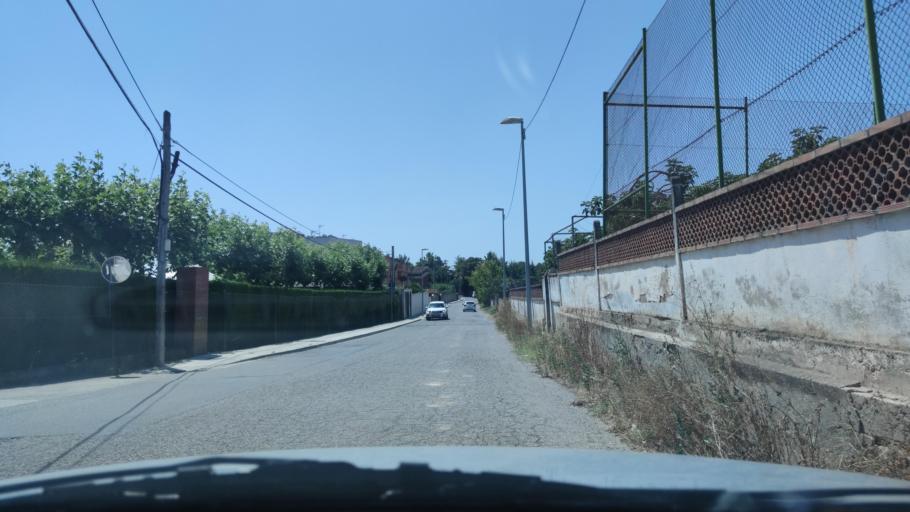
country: ES
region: Catalonia
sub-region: Provincia de Lleida
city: Lleida
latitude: 41.6328
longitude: 0.5992
